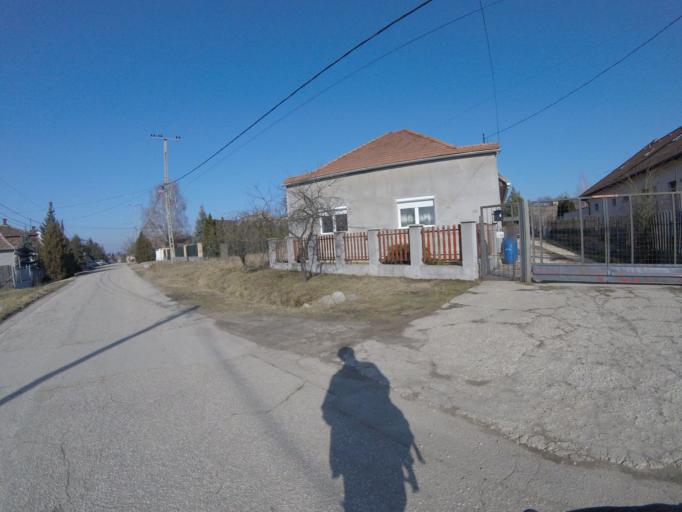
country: HU
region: Komarom-Esztergom
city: Oroszlany
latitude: 47.4797
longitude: 18.3295
